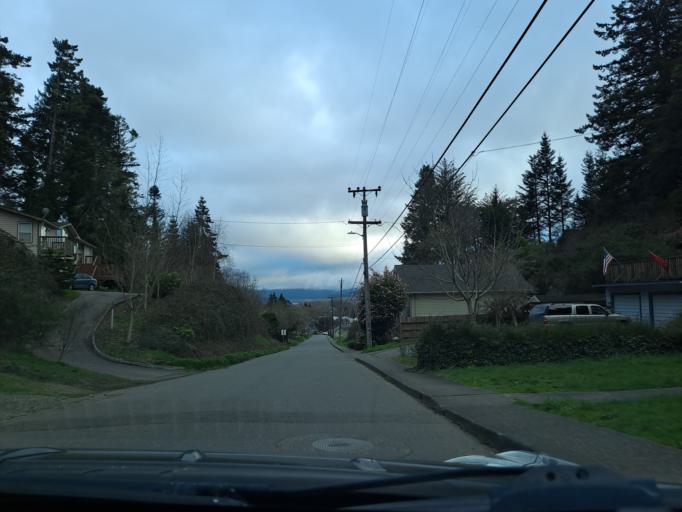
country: US
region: California
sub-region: Humboldt County
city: Fortuna
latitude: 40.6026
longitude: -124.1609
